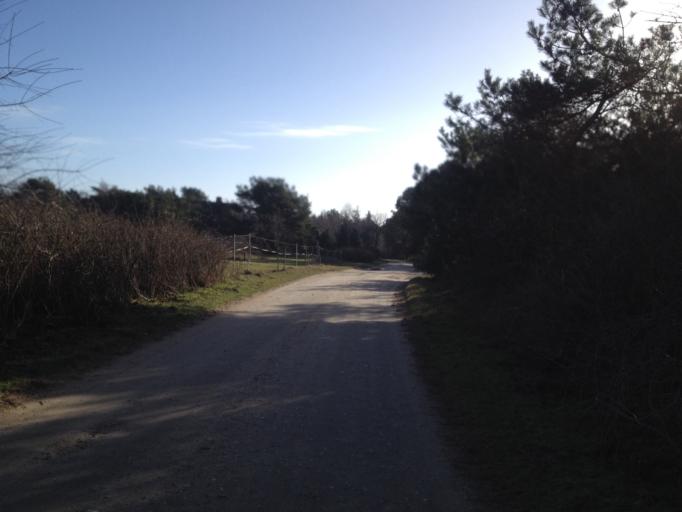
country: DE
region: Schleswig-Holstein
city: Nebel
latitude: 54.6440
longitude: 8.3478
